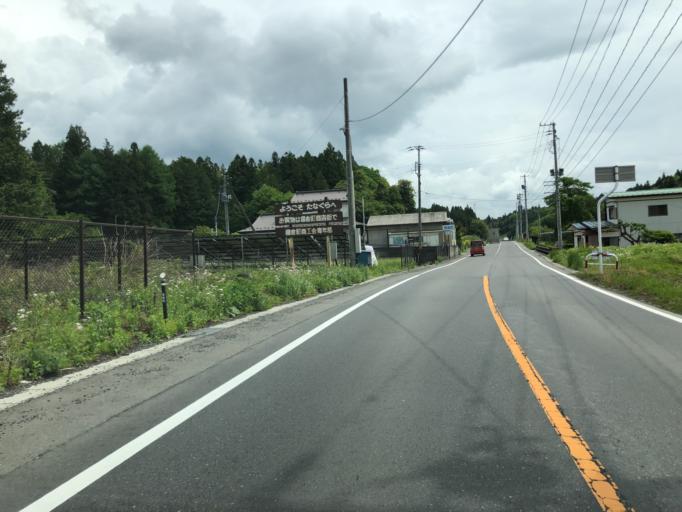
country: JP
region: Fukushima
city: Ishikawa
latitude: 37.0757
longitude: 140.3607
